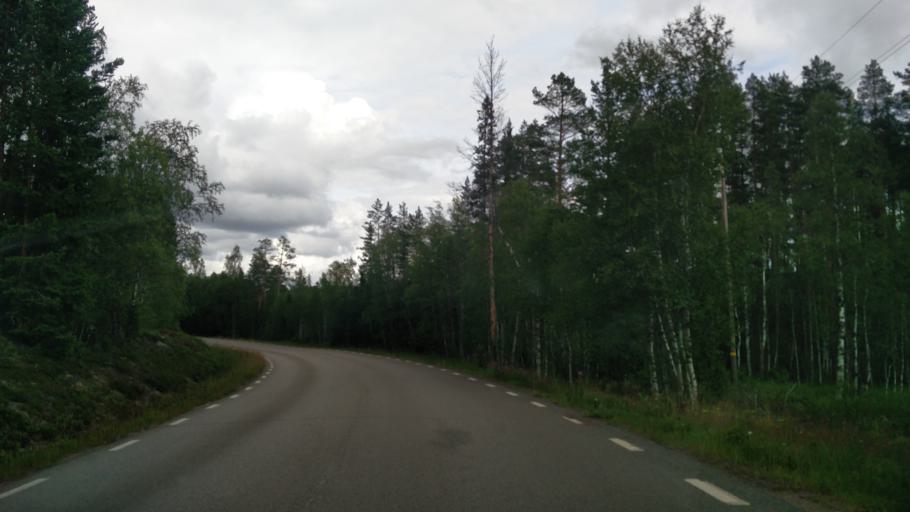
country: NO
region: Hedmark
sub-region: Trysil
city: Innbygda
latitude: 61.1537
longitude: 12.8118
